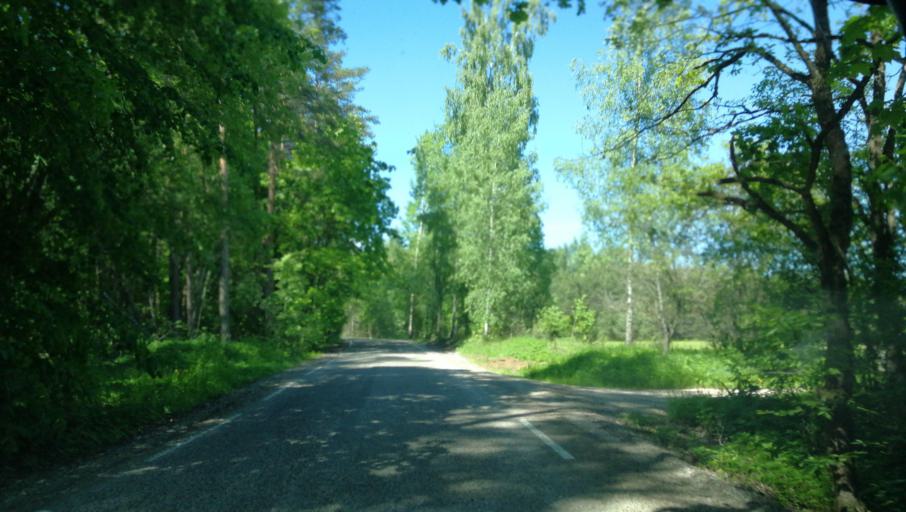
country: LV
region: Kekava
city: Kekava
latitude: 56.8682
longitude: 24.2306
